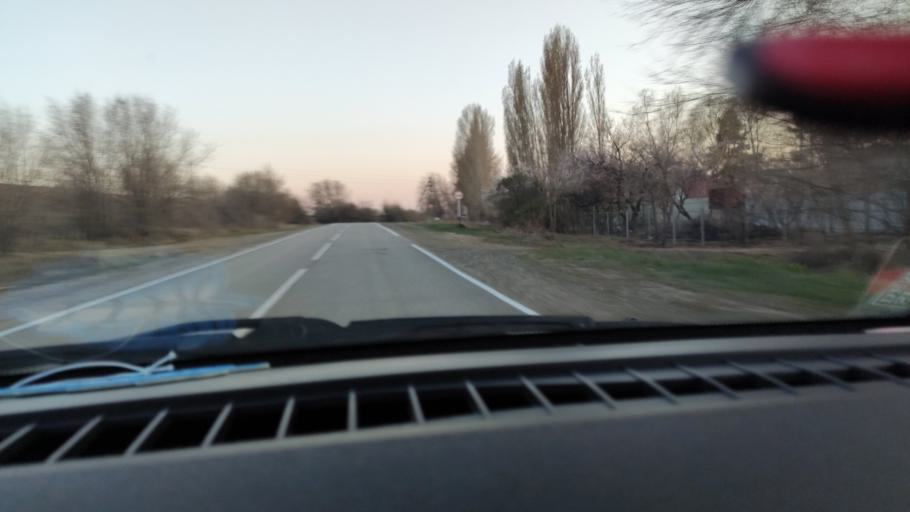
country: RU
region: Saratov
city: Privolzhskiy
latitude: 51.2218
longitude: 45.9203
